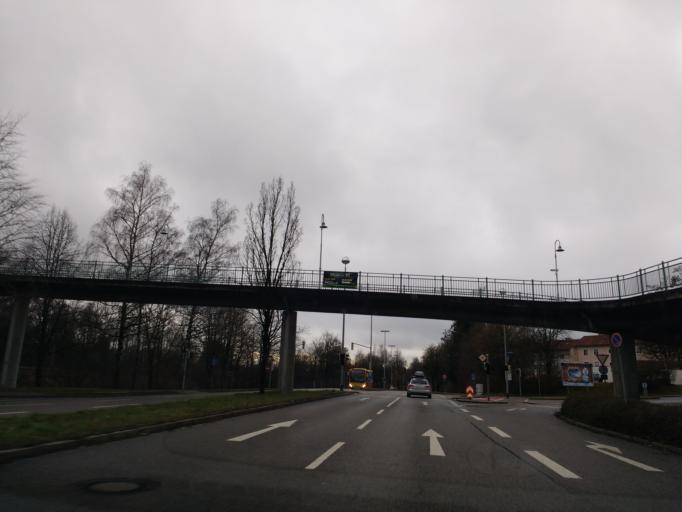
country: DE
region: Bavaria
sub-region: Swabia
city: Kempten (Allgaeu)
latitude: 47.7185
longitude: 10.3308
